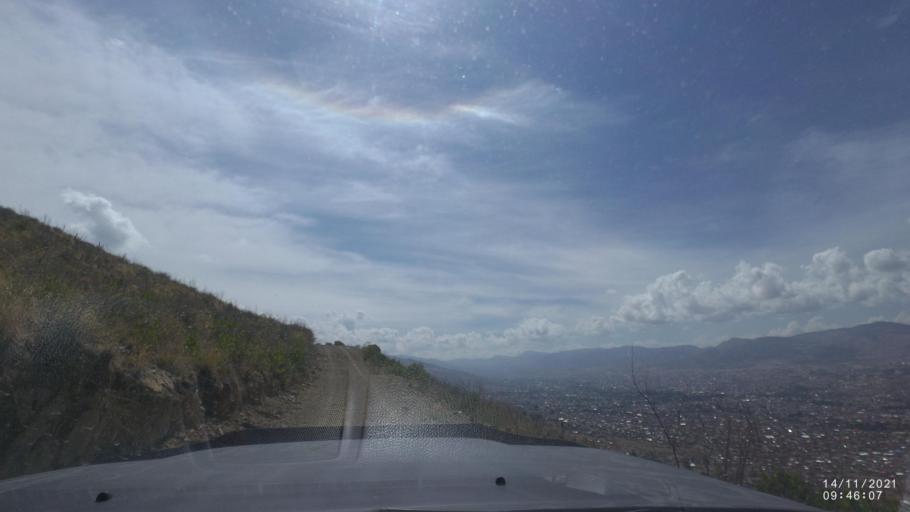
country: BO
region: Cochabamba
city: Cochabamba
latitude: -17.3626
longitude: -66.0889
